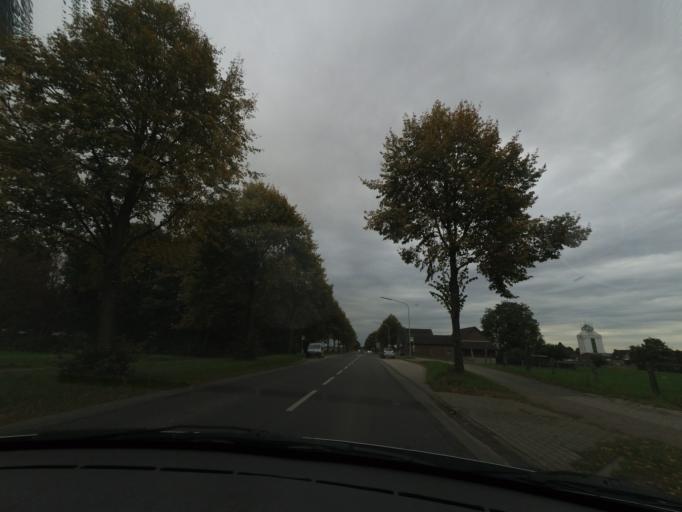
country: DE
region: North Rhine-Westphalia
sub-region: Regierungsbezirk Dusseldorf
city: Korschenbroich
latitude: 51.1647
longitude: 6.5357
